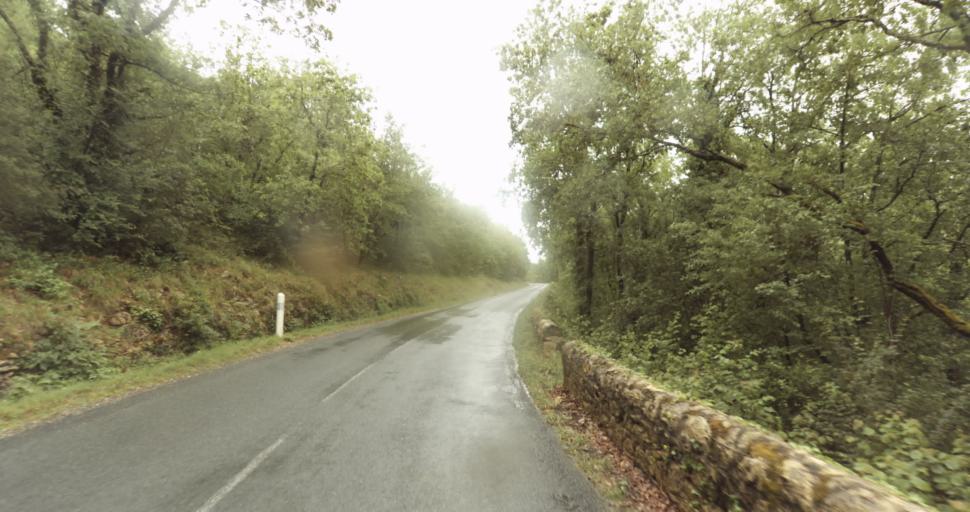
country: FR
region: Aquitaine
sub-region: Departement de la Dordogne
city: Beaumont-du-Perigord
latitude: 44.7714
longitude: 0.8049
